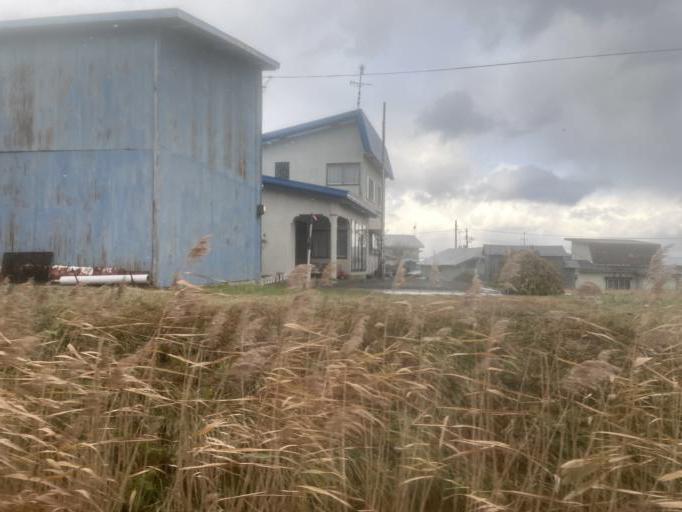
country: JP
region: Aomori
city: Shimokizukuri
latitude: 41.1809
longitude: 140.4667
